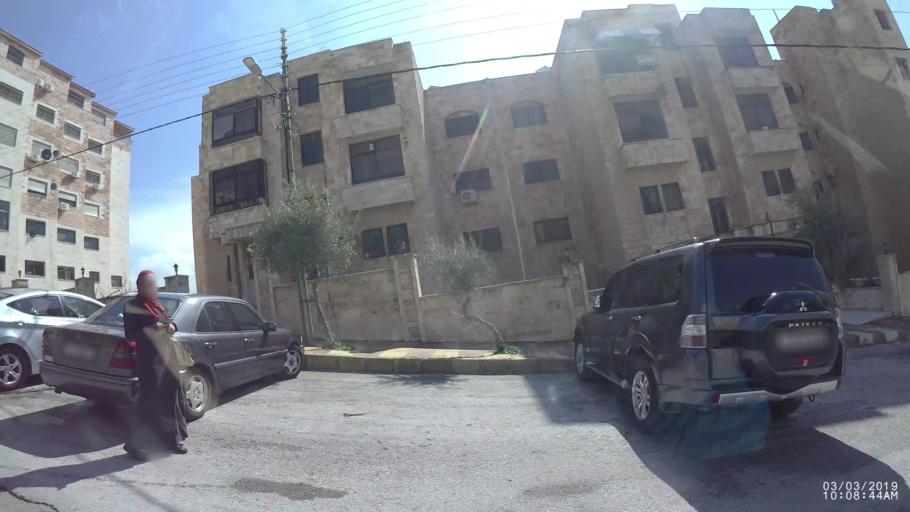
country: JO
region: Amman
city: Al Jubayhah
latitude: 31.9905
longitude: 35.8993
